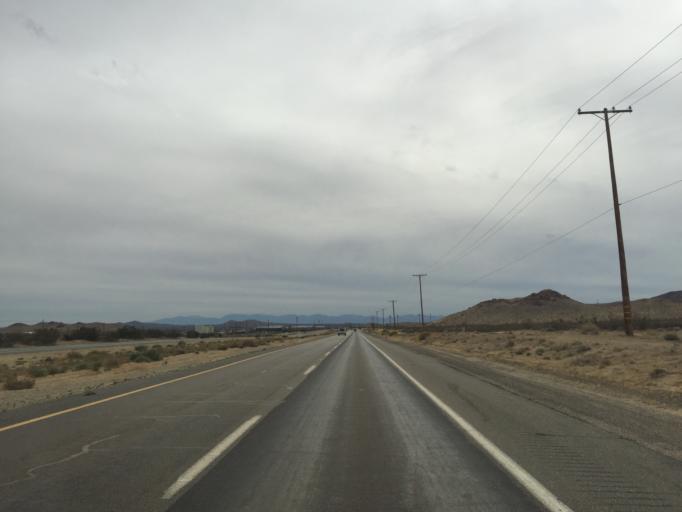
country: US
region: California
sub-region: Kern County
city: Mojave
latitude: 35.0146
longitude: -118.1627
